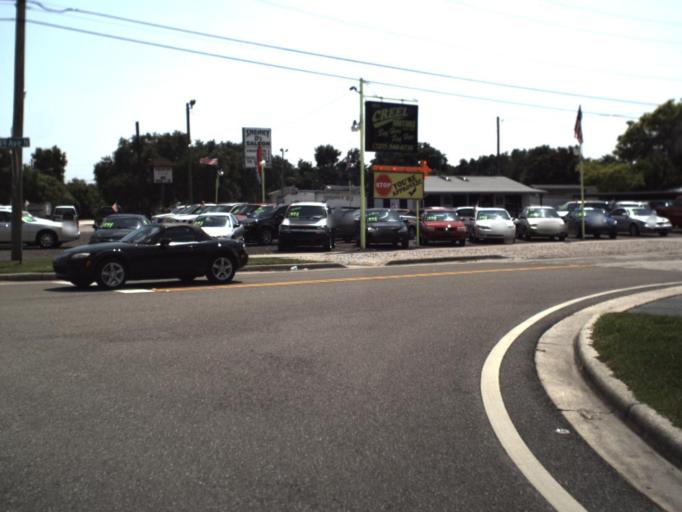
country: US
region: Florida
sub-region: Pinellas County
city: Kenneth City
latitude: 27.8166
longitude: -82.7287
